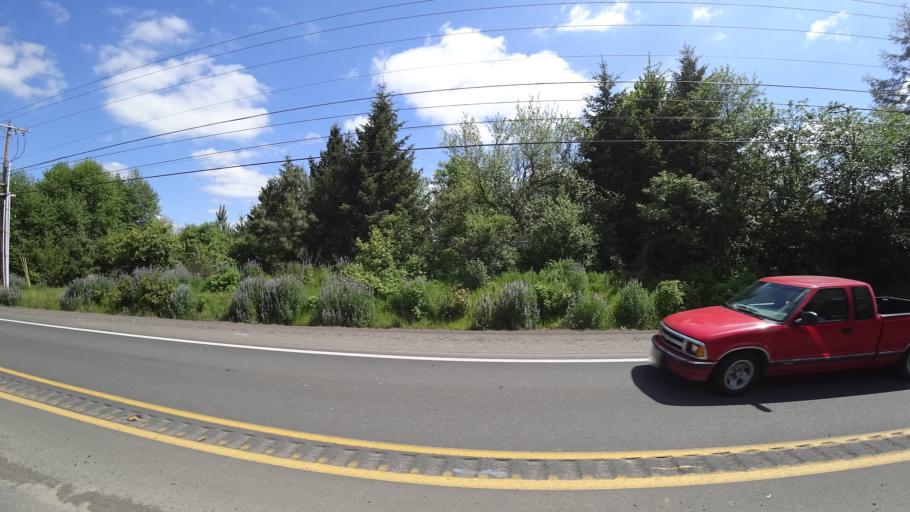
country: US
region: Oregon
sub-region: Washington County
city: Hillsboro
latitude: 45.5020
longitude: -122.9910
